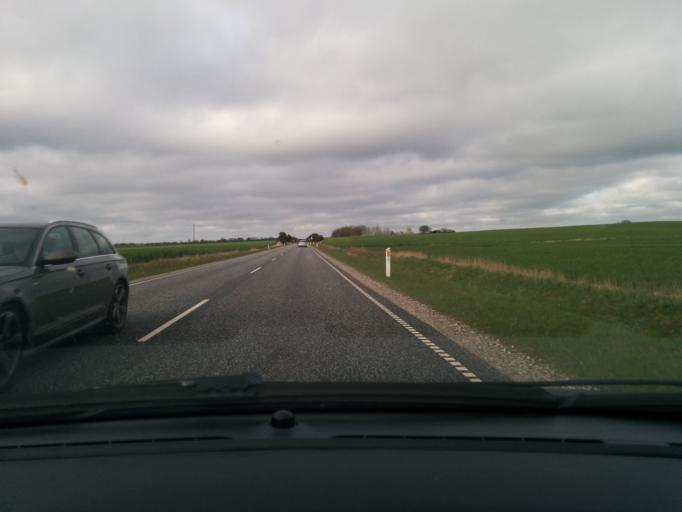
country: DK
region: Central Jutland
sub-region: Favrskov Kommune
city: Hammel
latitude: 56.2266
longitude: 9.8540
